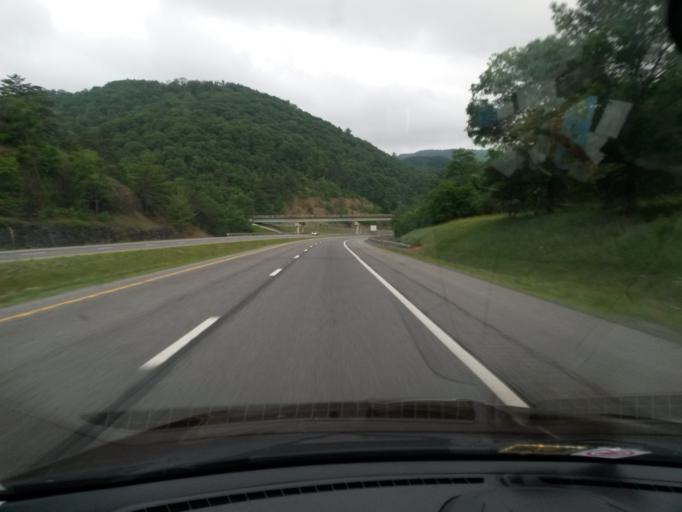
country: US
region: West Virginia
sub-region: Greenbrier County
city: White Sulphur Springs
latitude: 37.7831
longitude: -80.2303
